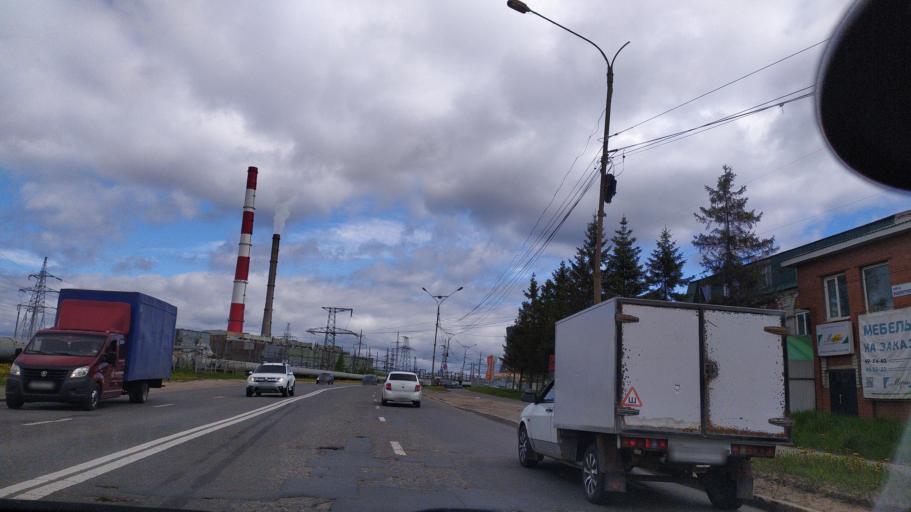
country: RU
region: Chuvashia
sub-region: Cheboksarskiy Rayon
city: Cheboksary
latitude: 56.1184
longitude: 47.3019
